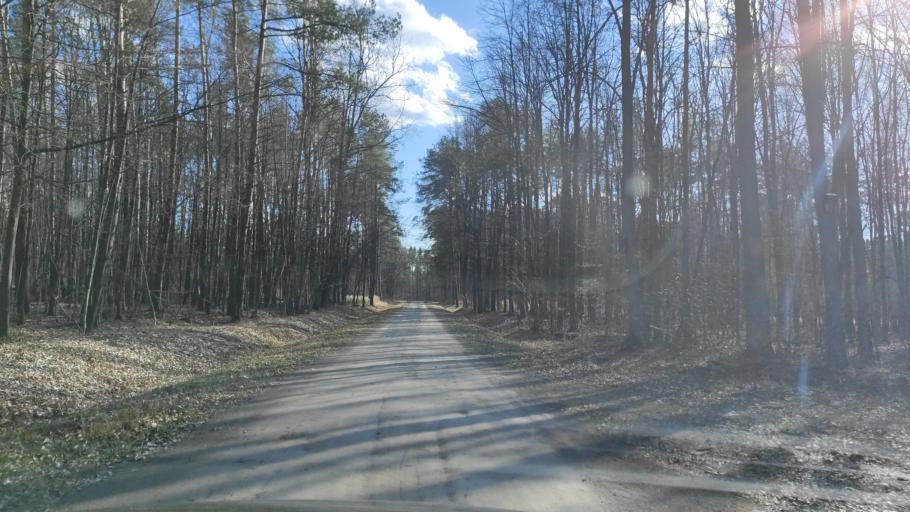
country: PL
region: Masovian Voivodeship
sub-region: Powiat radomski
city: Jedlnia-Letnisko
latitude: 51.4452
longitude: 21.2935
